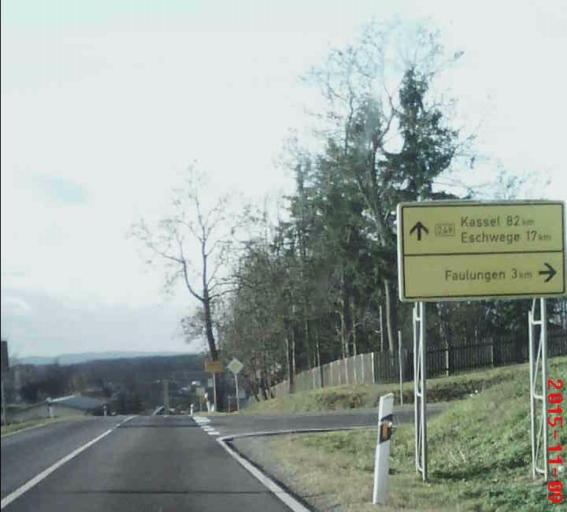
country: DE
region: Thuringia
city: Katharinenberg
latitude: 51.1849
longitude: 10.2645
